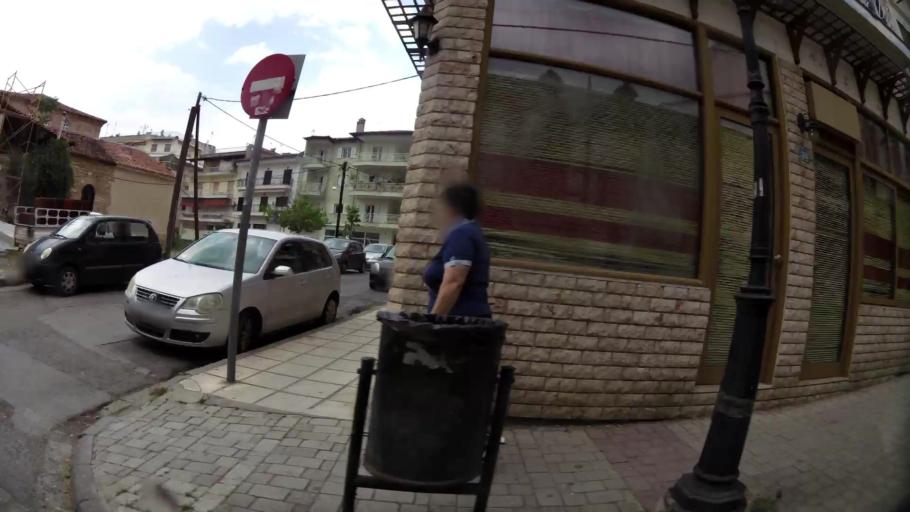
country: GR
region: Central Macedonia
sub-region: Nomos Imathias
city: Veroia
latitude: 40.5221
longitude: 22.2012
